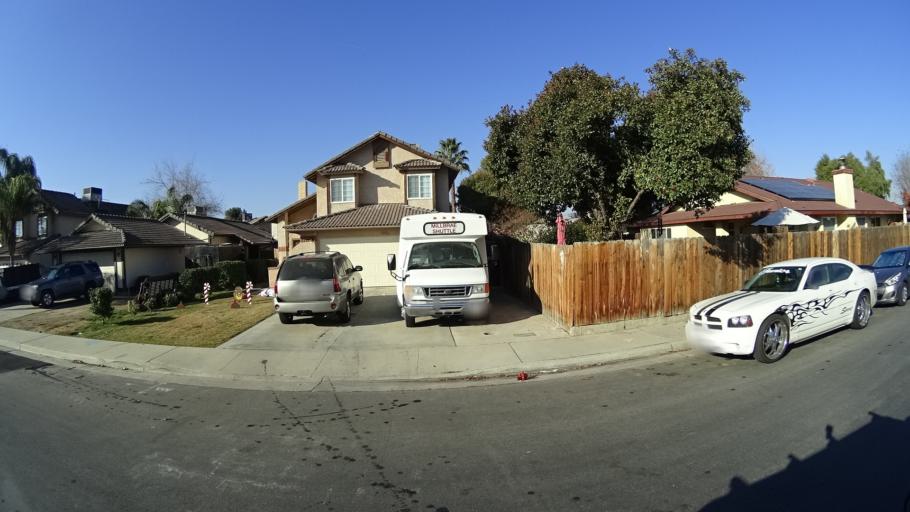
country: US
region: California
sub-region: Kern County
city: Greenfield
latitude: 35.3066
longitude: -119.0174
